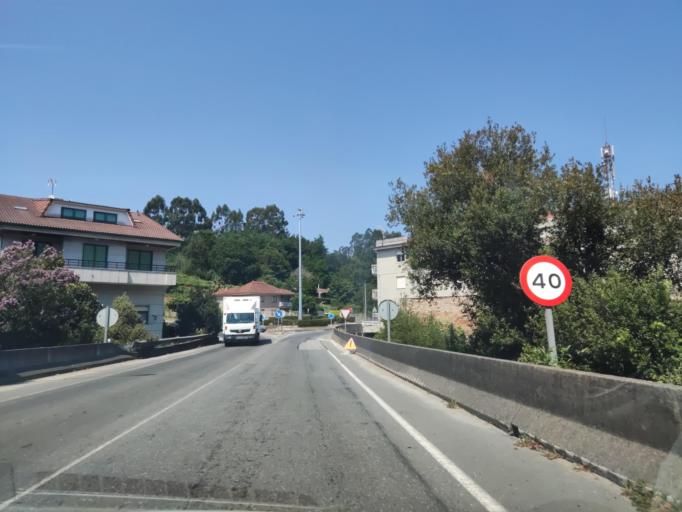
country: ES
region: Galicia
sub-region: Provincia de Pontevedra
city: Redondela
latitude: 42.2778
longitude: -8.6115
